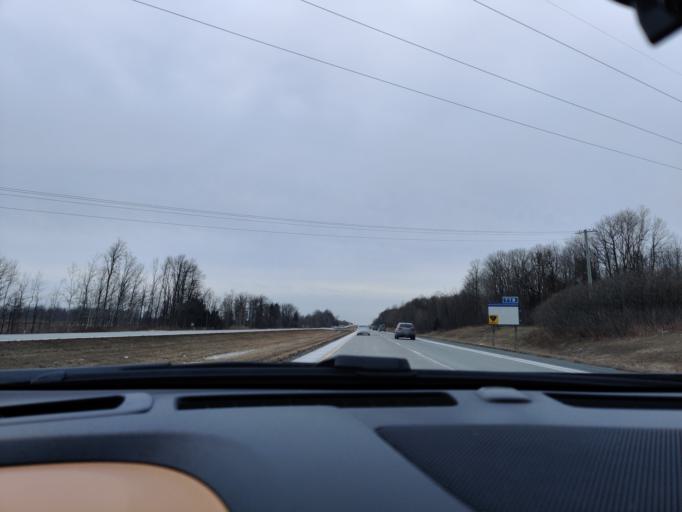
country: US
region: New York
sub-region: St. Lawrence County
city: Massena
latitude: 45.0538
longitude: -74.8872
